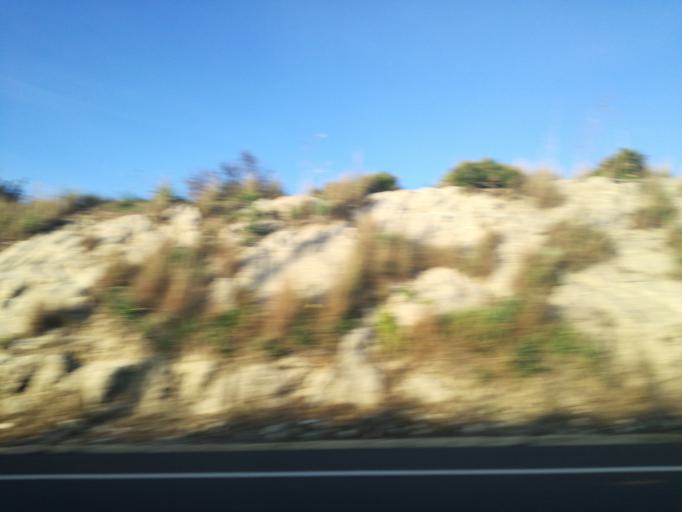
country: IT
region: Sicily
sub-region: Catania
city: San Michele di Ganzaria
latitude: 37.2156
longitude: 14.4189
